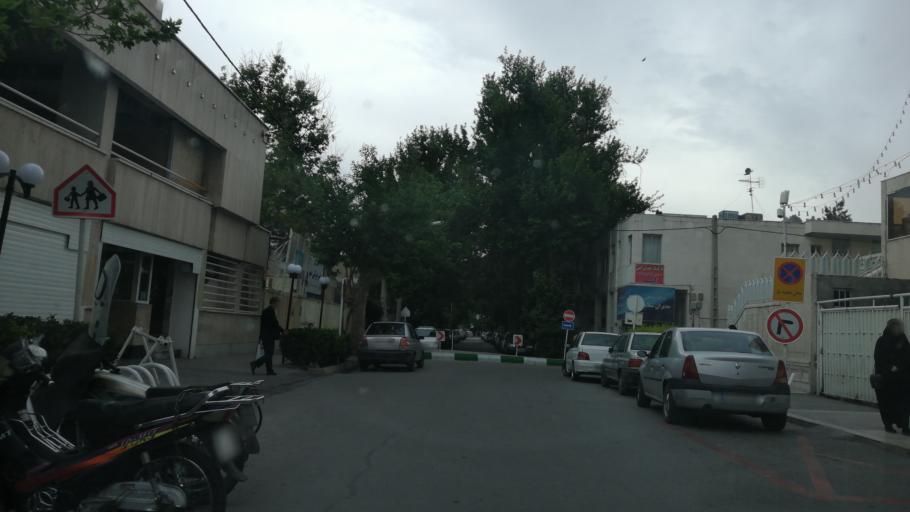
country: IR
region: Razavi Khorasan
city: Mashhad
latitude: 36.2901
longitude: 59.5853
